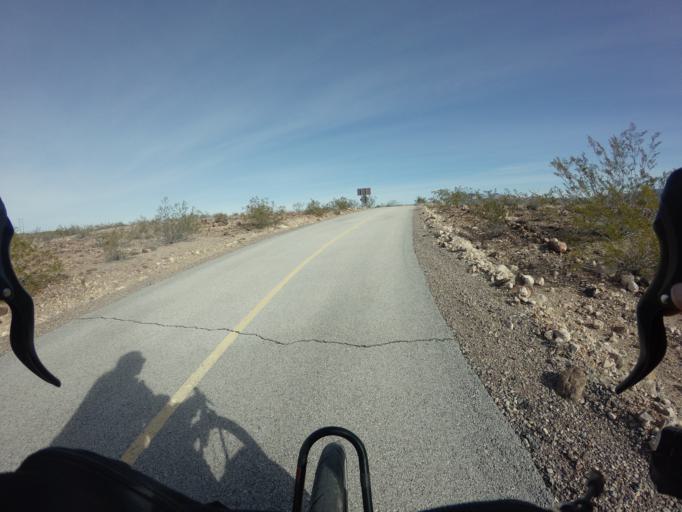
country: US
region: Nevada
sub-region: Clark County
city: Boulder City
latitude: 36.0732
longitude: -114.8119
